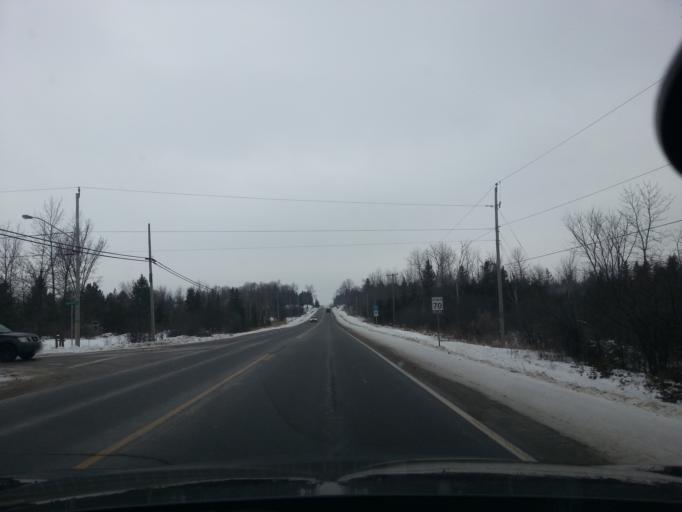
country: CA
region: Ontario
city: Carleton Place
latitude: 45.2441
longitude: -76.1678
